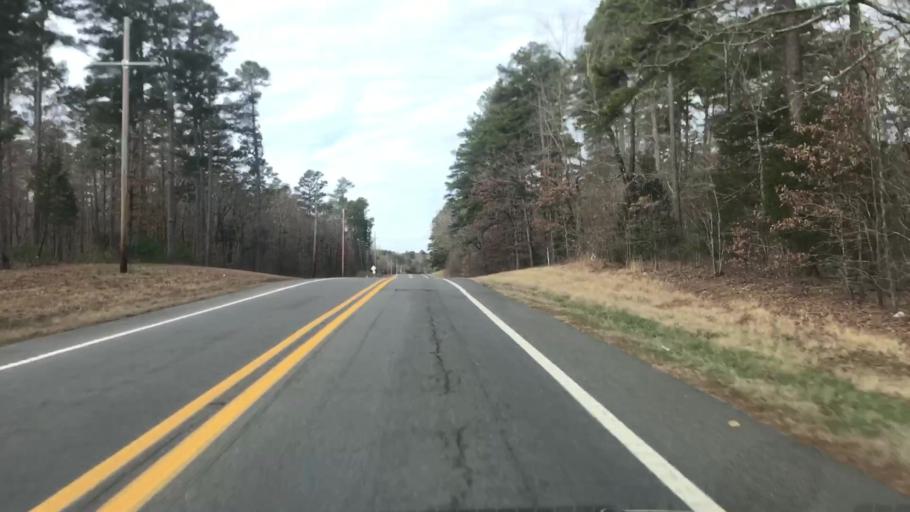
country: US
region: Arkansas
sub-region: Montgomery County
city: Mount Ida
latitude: 34.6087
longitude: -93.6762
